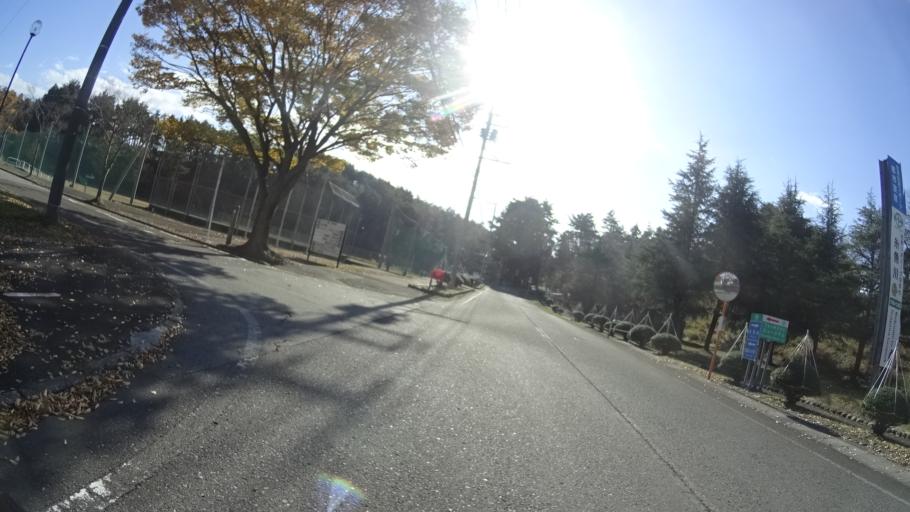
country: JP
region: Niigata
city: Itoigawa
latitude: 37.0247
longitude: 137.8622
